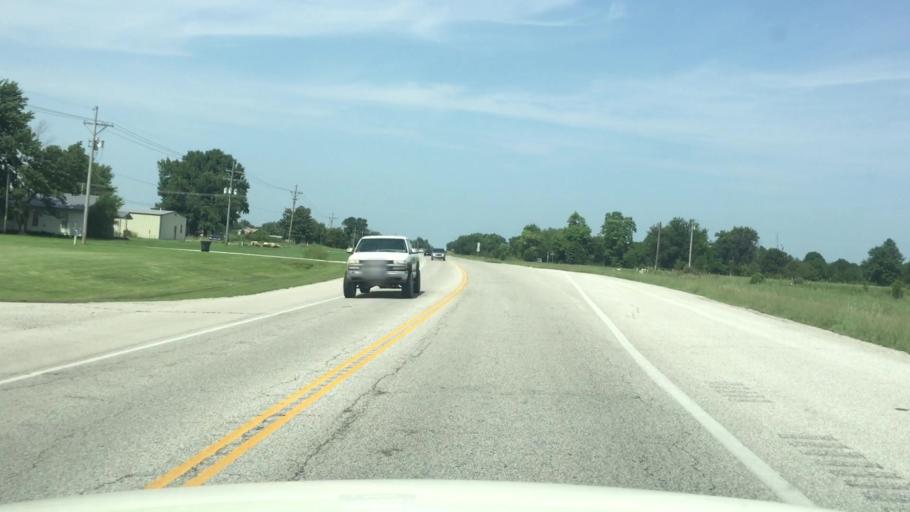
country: US
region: Kansas
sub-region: Cherokee County
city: Galena
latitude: 37.0881
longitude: -94.7043
